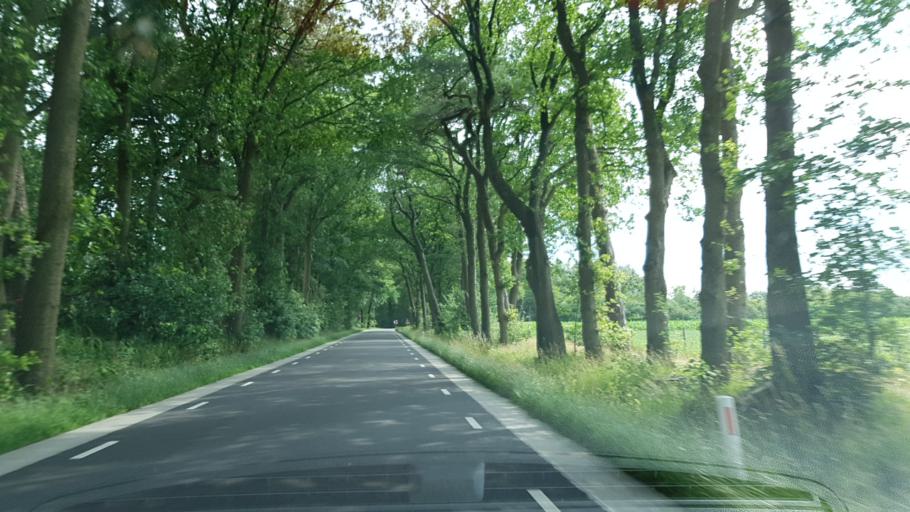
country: NL
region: Gelderland
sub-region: Gemeente Barneveld
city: Garderen
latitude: 52.2773
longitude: 5.7302
